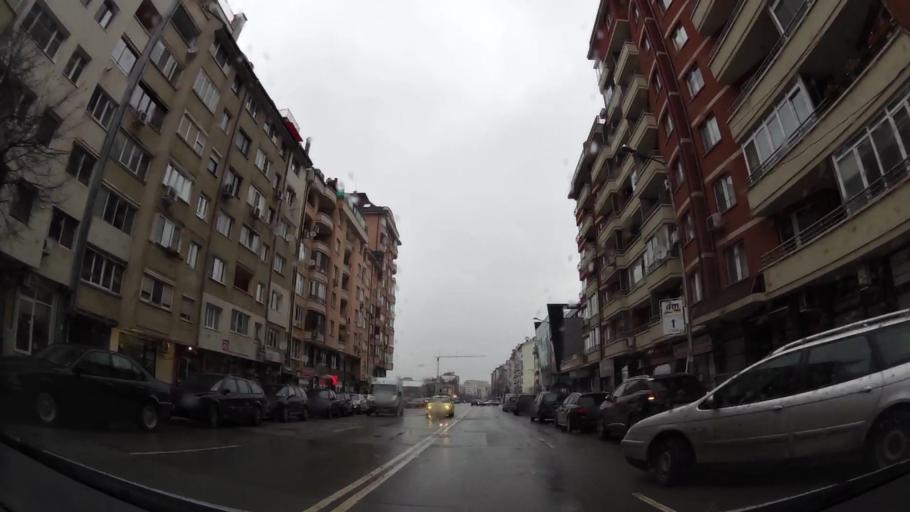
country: BG
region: Sofia-Capital
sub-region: Stolichna Obshtina
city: Sofia
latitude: 42.6344
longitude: 23.3750
